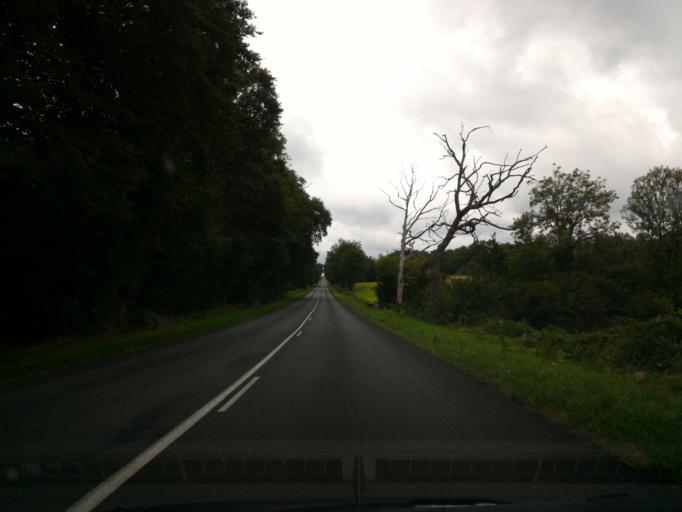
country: FR
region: Poitou-Charentes
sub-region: Departement de la Charente
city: Etagnac
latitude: 45.8867
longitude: 0.7662
